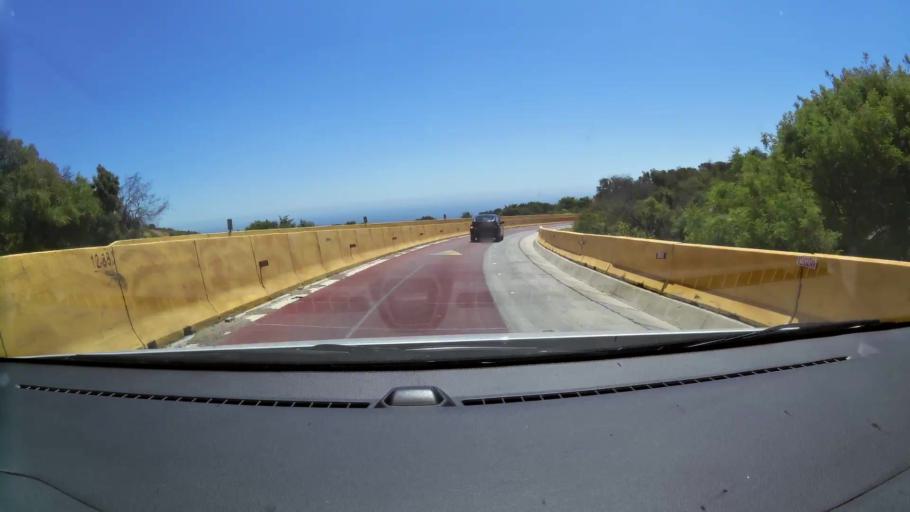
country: CL
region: Valparaiso
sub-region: Provincia de Valparaiso
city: Valparaiso
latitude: -33.0594
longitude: -71.6536
